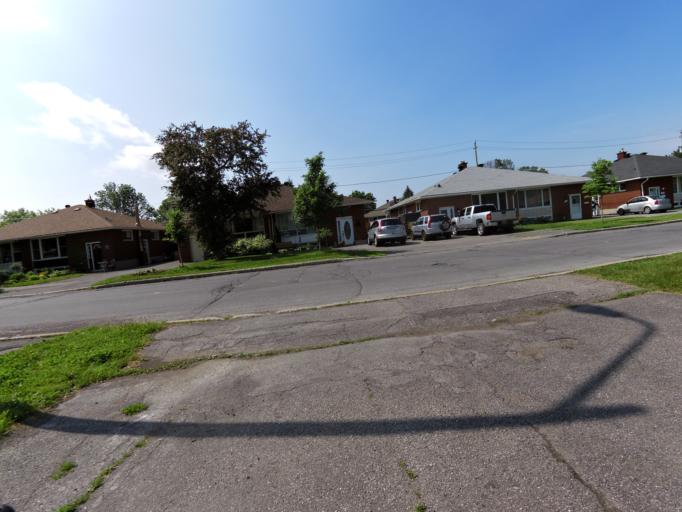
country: CA
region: Ontario
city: Bells Corners
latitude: 45.3511
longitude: -75.7718
